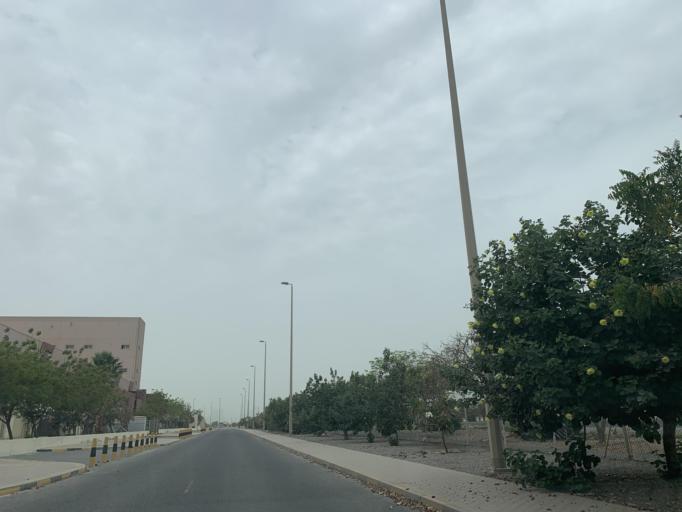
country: BH
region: Muharraq
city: Al Hadd
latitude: 26.2247
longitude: 50.6702
